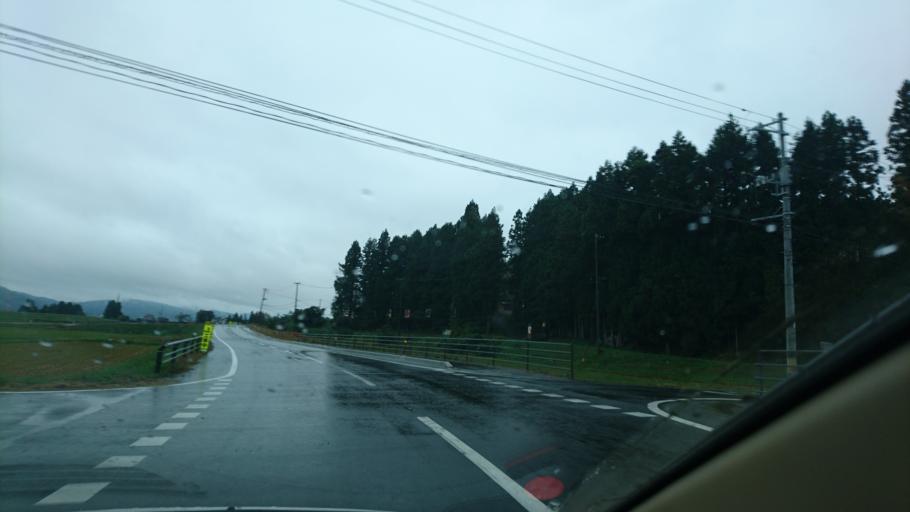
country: JP
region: Iwate
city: Ichinoseki
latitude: 38.9758
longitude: 141.1027
